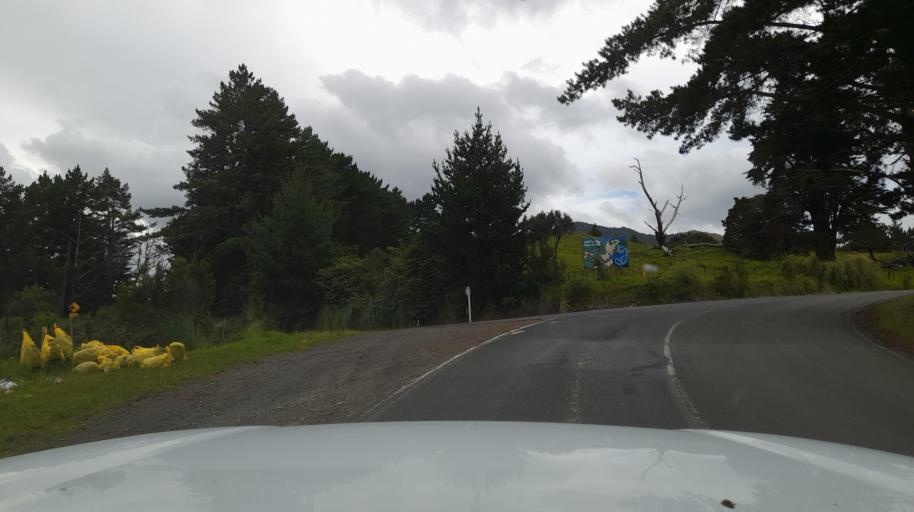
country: NZ
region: Northland
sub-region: Far North District
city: Kaitaia
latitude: -35.3120
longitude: 173.3414
